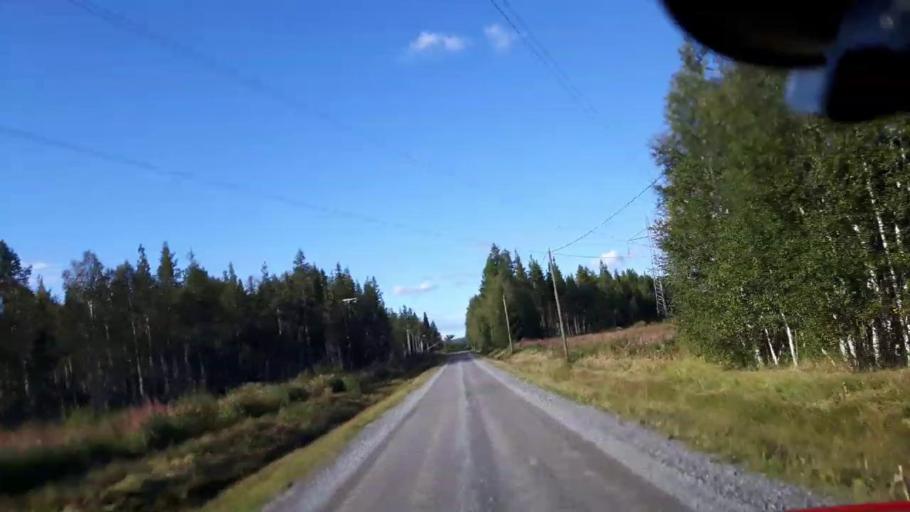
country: SE
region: Jaemtland
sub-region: Ragunda Kommun
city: Hammarstrand
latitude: 63.5166
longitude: 16.0568
